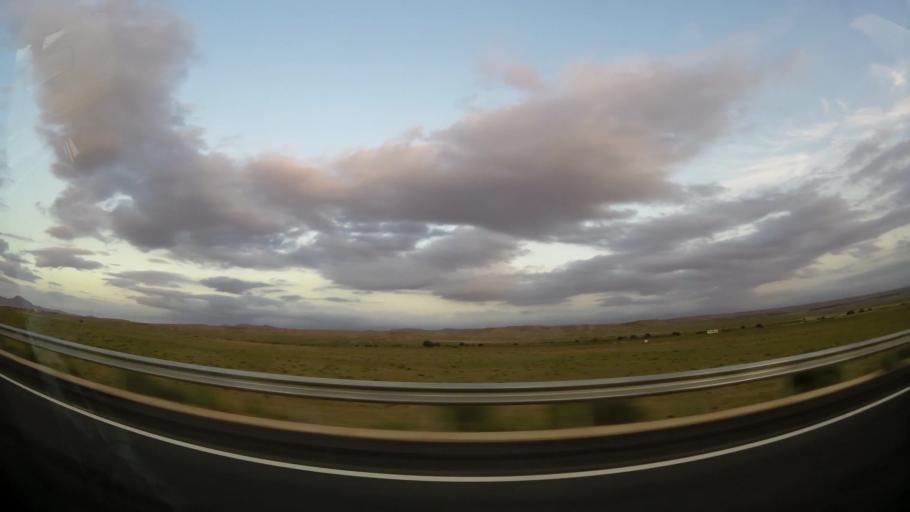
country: MA
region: Oriental
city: Taourirt
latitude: 34.5929
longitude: -2.7829
